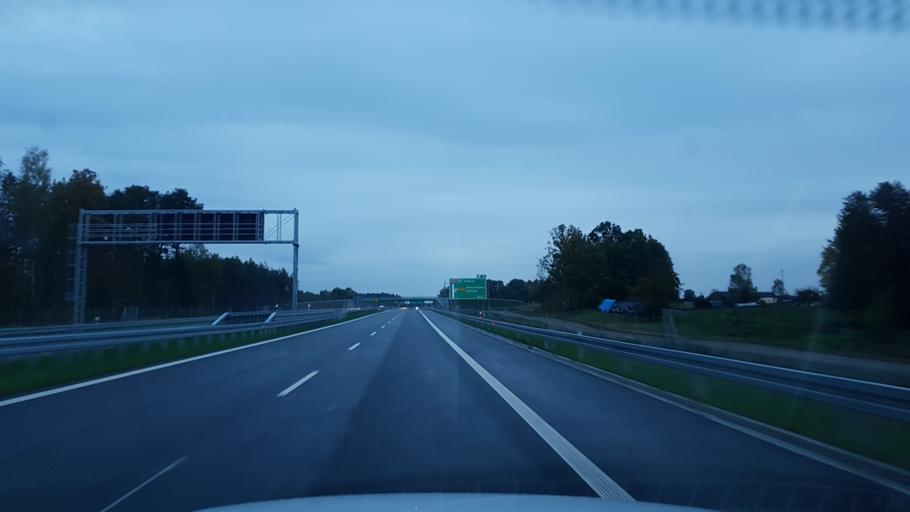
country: PL
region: West Pomeranian Voivodeship
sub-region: Powiat gryficki
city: Brojce
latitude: 53.9337
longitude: 15.3927
